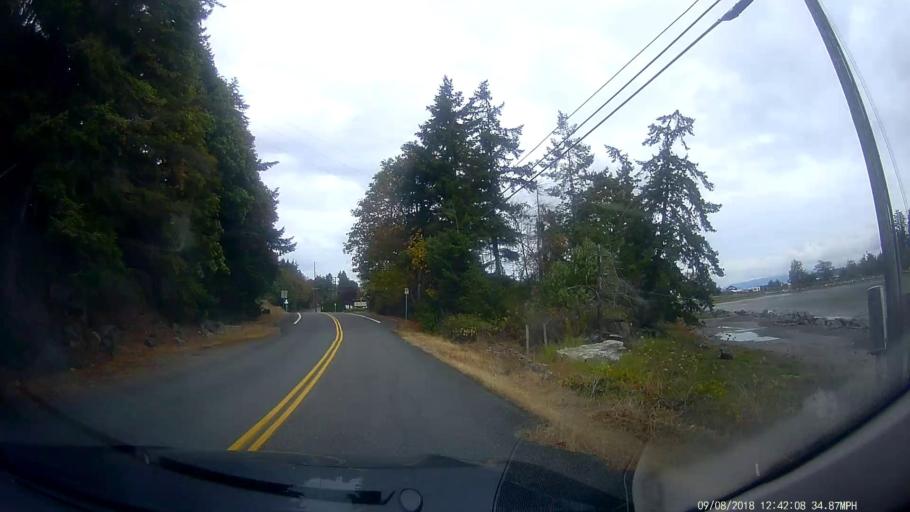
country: US
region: Washington
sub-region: Skagit County
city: Anacortes
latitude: 48.4812
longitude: -122.5931
